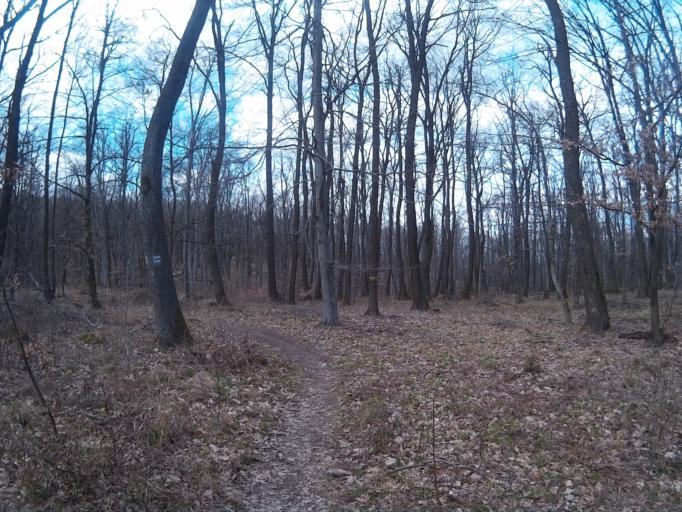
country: HU
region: Pest
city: Kosd
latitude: 47.8352
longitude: 19.1437
